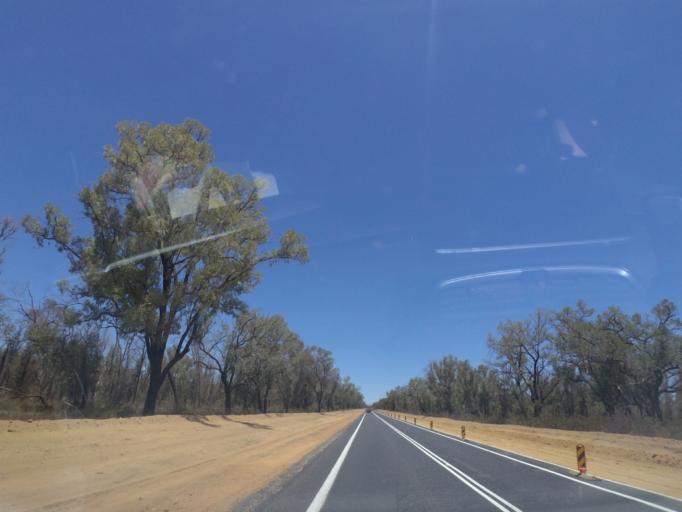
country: AU
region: New South Wales
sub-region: Warrumbungle Shire
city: Coonabarabran
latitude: -30.9325
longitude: 149.4279
